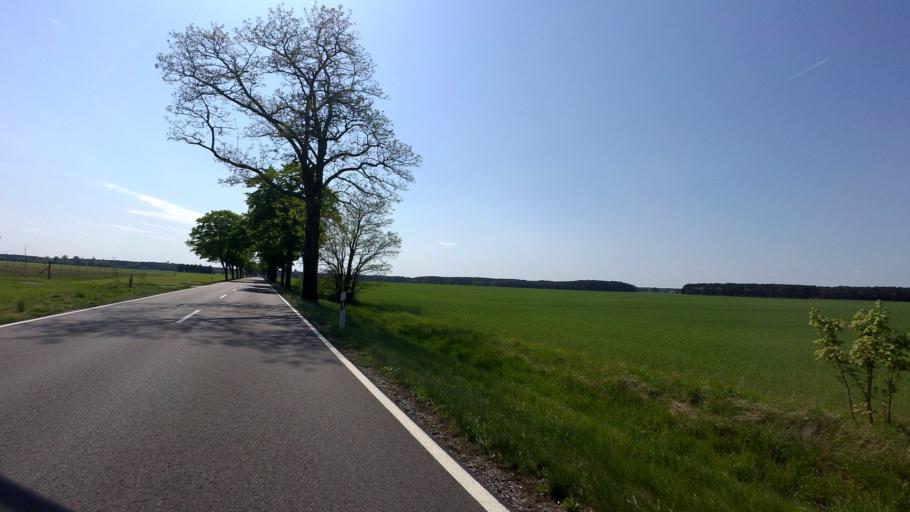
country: DE
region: Brandenburg
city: Neu Zauche
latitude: 52.0140
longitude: 14.0648
